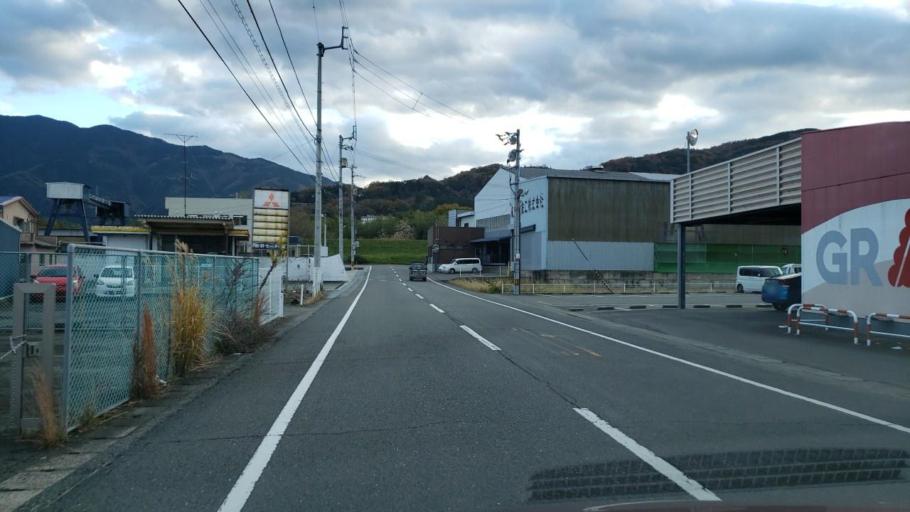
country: JP
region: Tokushima
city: Wakimachi
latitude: 34.0624
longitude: 134.1635
